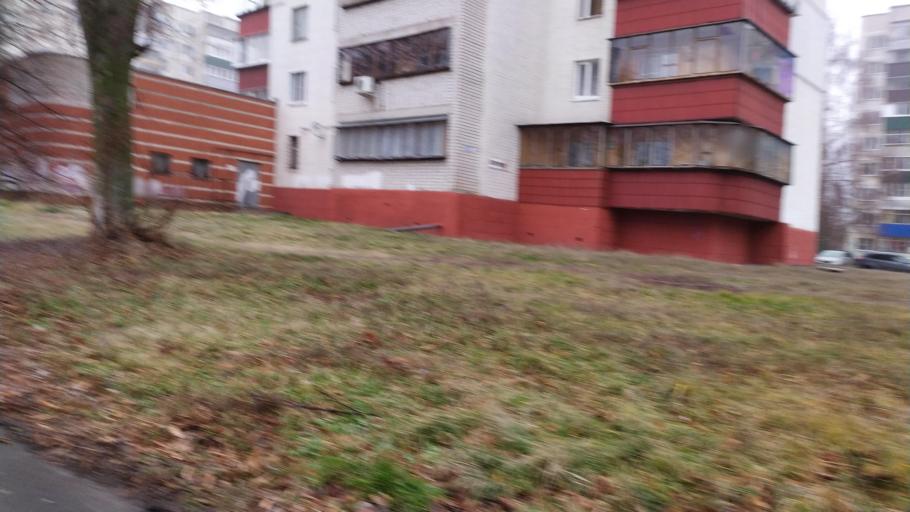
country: RU
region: Kursk
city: Kursk
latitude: 51.7428
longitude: 36.1347
